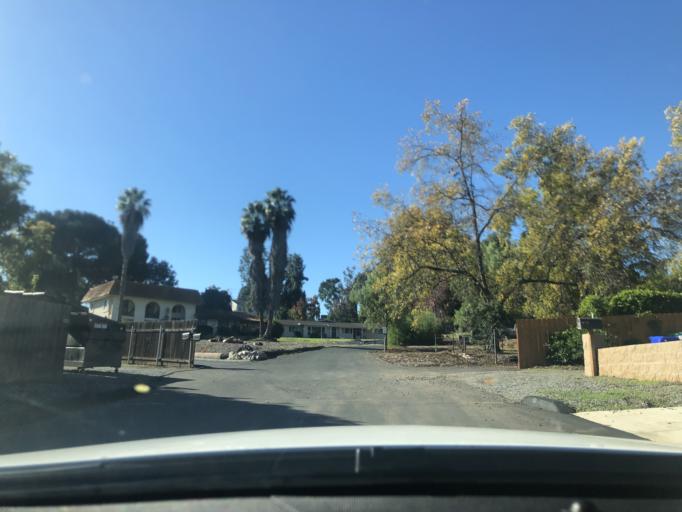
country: US
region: California
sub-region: San Diego County
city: Rancho San Diego
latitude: 32.7717
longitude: -116.9397
